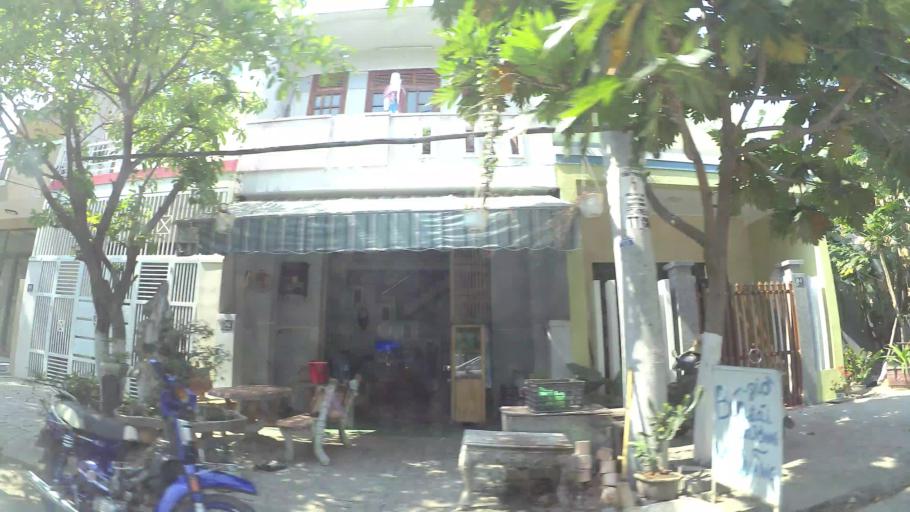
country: VN
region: Da Nang
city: Cam Le
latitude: 16.0105
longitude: 108.2027
